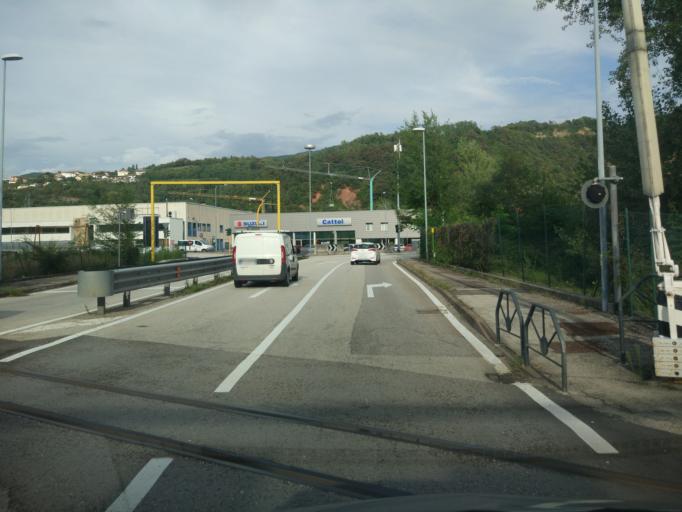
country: IT
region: Trentino-Alto Adige
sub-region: Provincia di Trento
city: Meano
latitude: 46.1184
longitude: 11.1052
